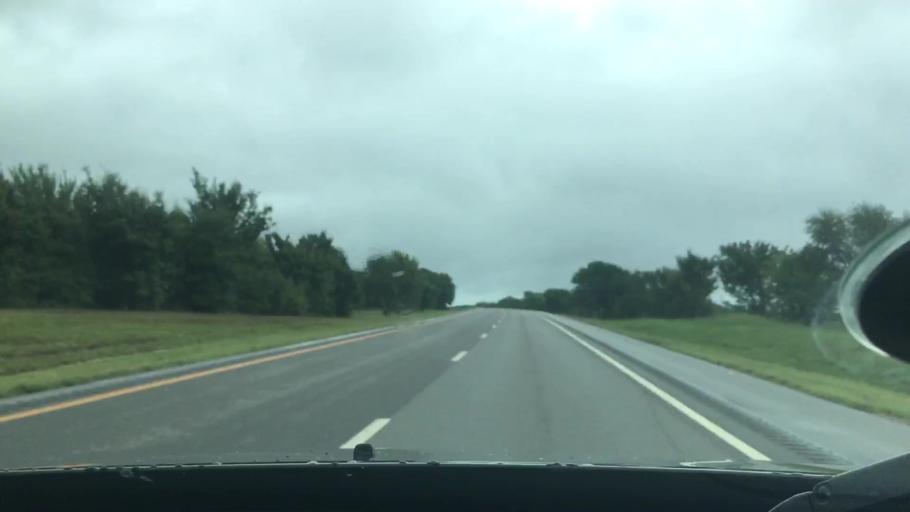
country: US
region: Oklahoma
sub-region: Okmulgee County
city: Henryetta
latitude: 35.4319
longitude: -95.8751
